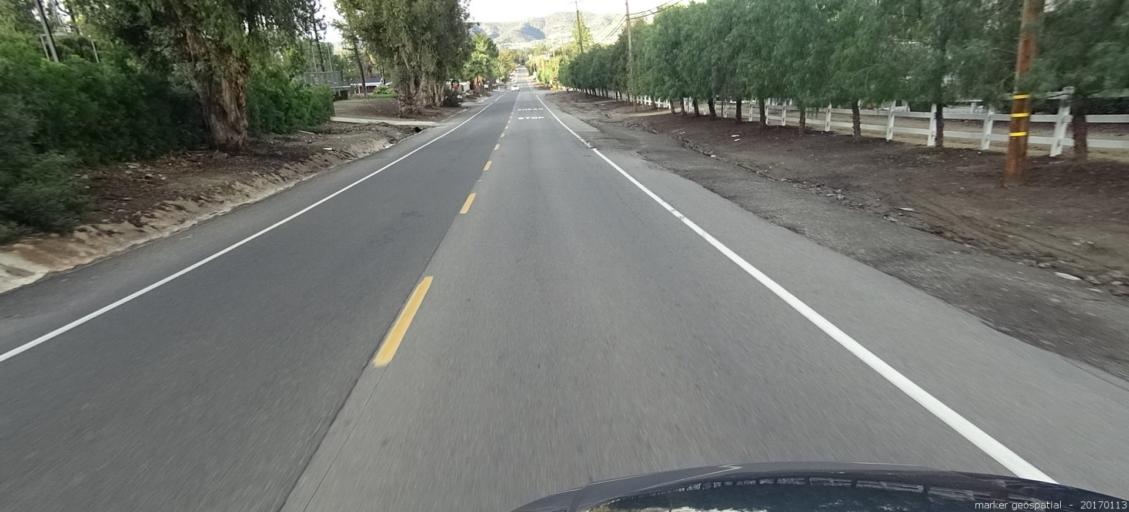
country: US
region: California
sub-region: Orange County
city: Villa Park
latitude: 33.7976
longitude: -117.7824
